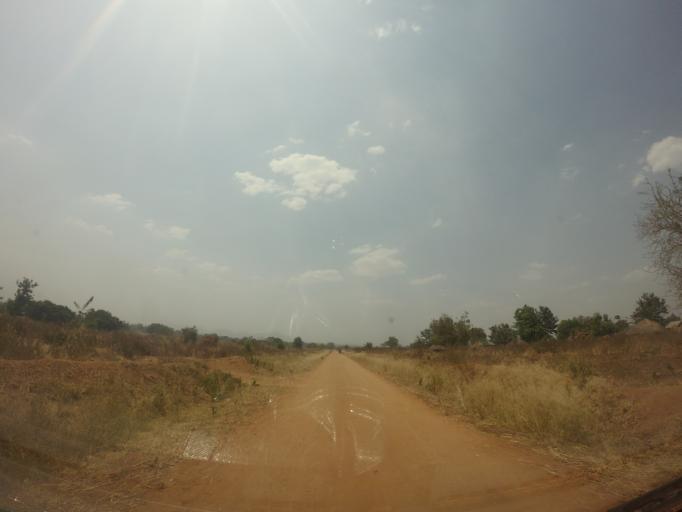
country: UG
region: Northern Region
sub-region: Arua District
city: Arua
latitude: 2.8840
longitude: 31.2096
